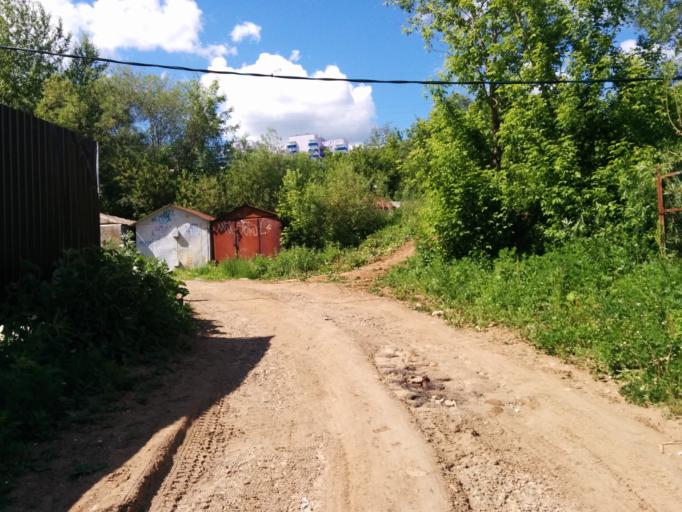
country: RU
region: Perm
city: Perm
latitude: 58.0119
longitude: 56.3030
